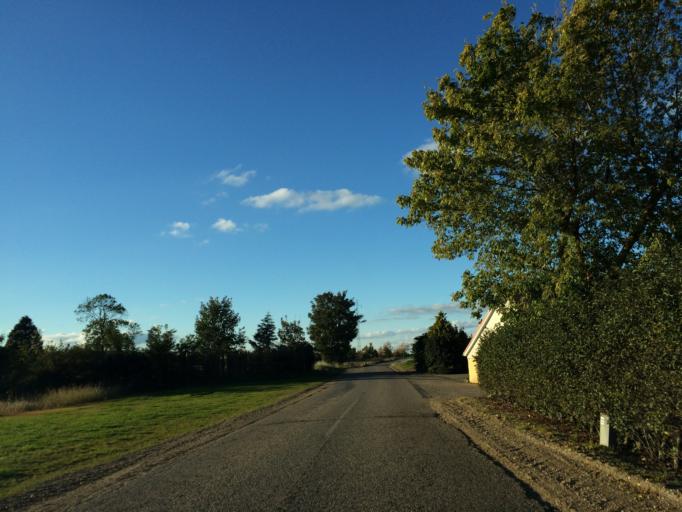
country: DK
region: Central Jutland
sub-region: Skanderborg Kommune
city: Ry
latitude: 56.1423
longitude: 9.7093
